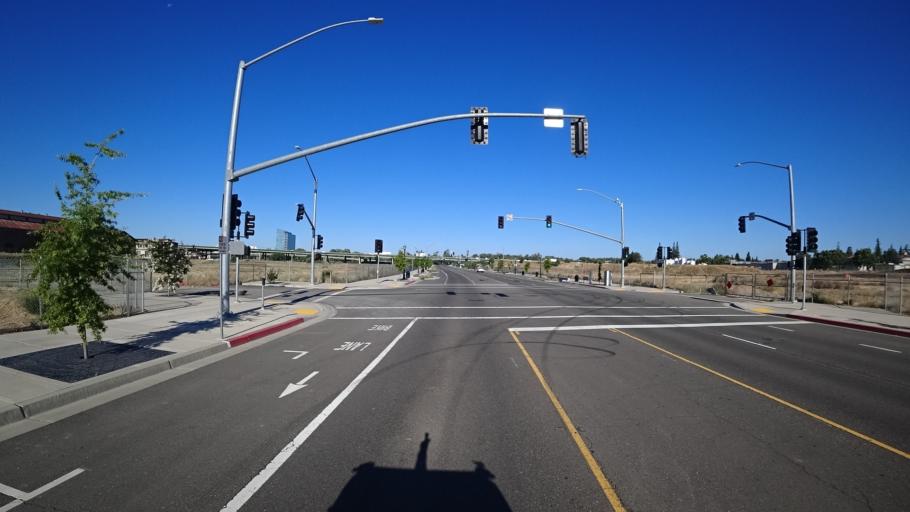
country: US
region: California
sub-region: Sacramento County
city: Sacramento
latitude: 38.5902
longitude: -121.4989
